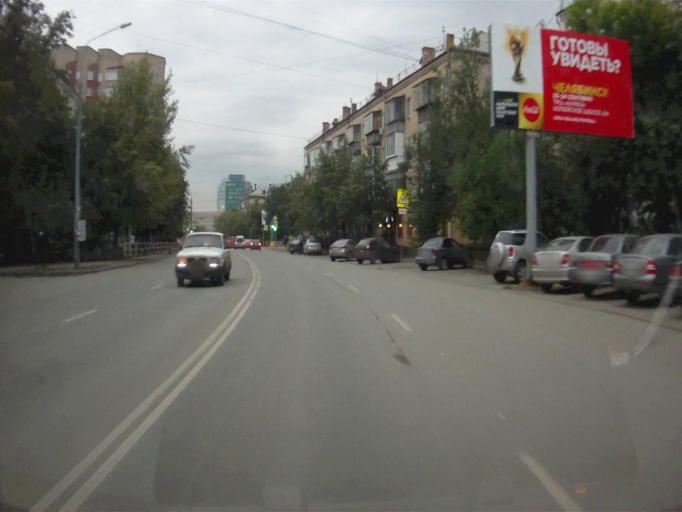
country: RU
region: Chelyabinsk
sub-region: Gorod Chelyabinsk
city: Chelyabinsk
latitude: 55.1542
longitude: 61.3987
